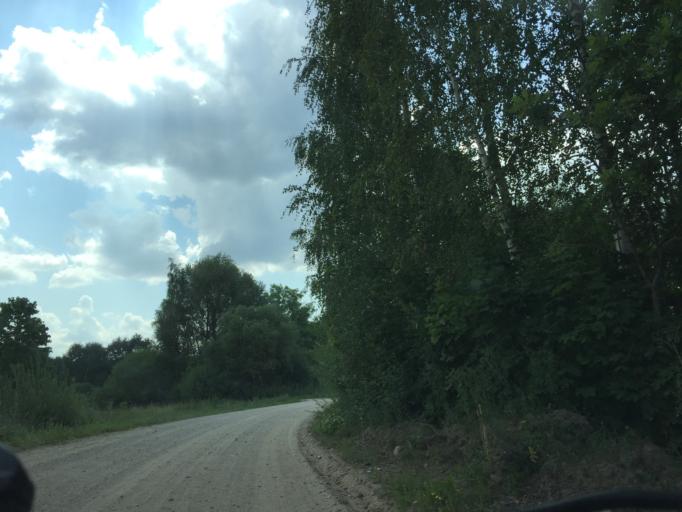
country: LT
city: Zagare
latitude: 56.3774
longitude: 23.1724
